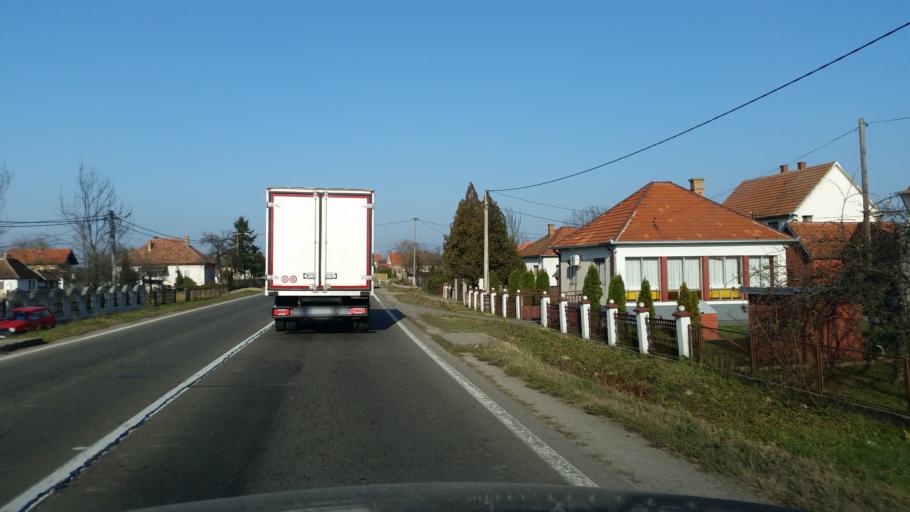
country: RS
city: Stepojevac
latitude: 44.5203
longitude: 20.2928
